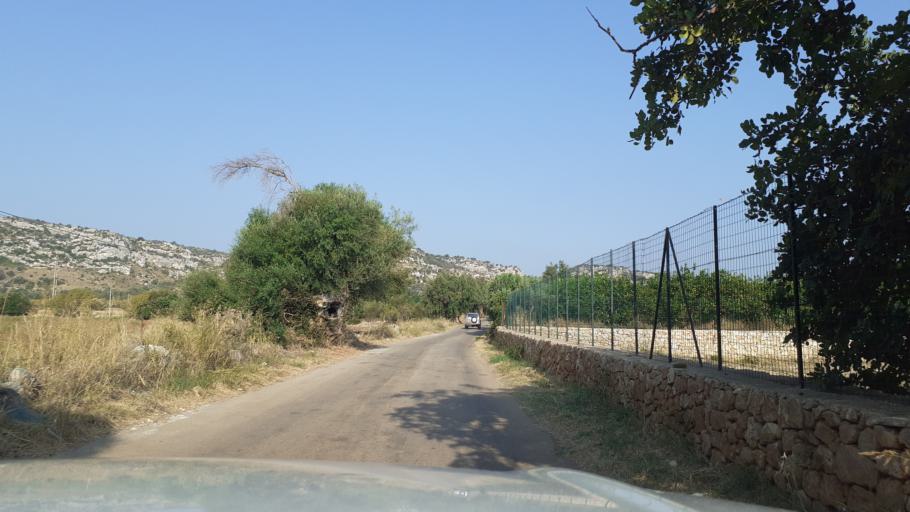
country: IT
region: Sicily
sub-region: Provincia di Siracusa
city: Cassibile
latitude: 36.9762
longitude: 15.1819
